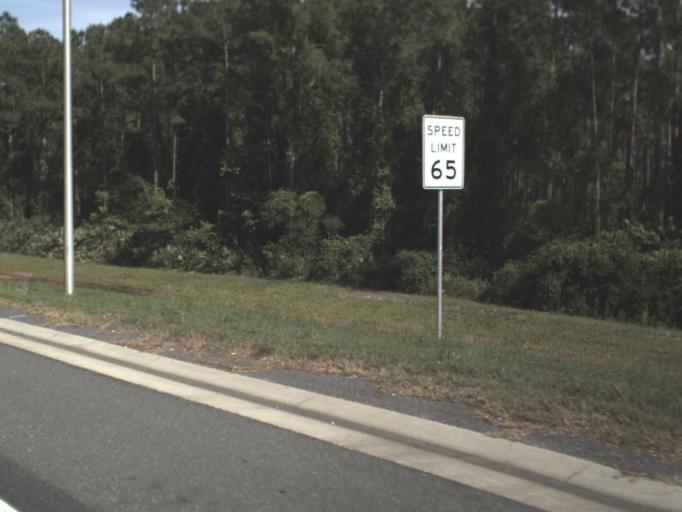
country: US
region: Florida
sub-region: Saint Johns County
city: Ponte Vedra Beach
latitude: 30.2512
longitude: -81.4823
